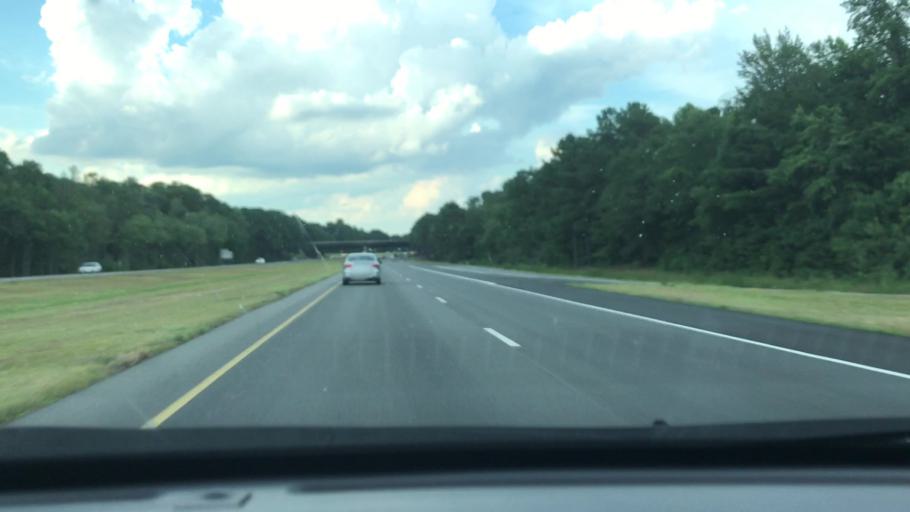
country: US
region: North Carolina
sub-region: Cumberland County
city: Eastover
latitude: 35.0846
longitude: -78.7855
